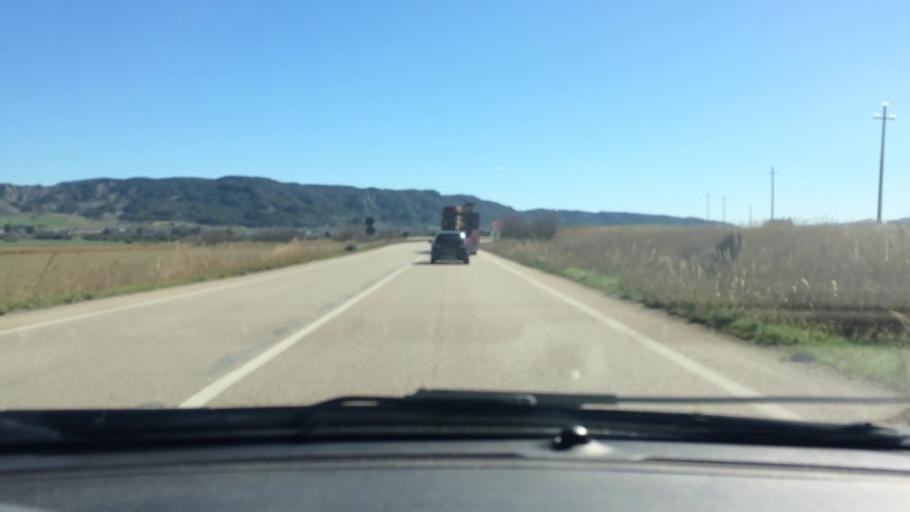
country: IT
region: Basilicate
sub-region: Provincia di Matera
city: Montescaglioso
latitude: 40.5311
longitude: 16.6166
